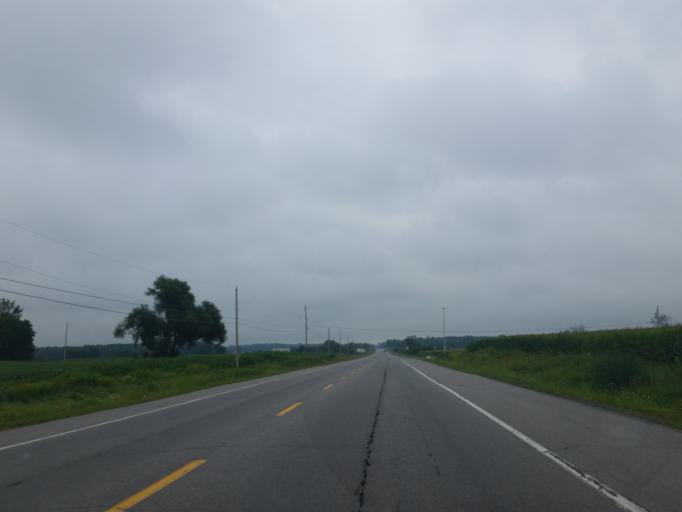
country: CA
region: Ontario
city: Clarence-Rockland
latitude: 45.4037
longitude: -75.3982
